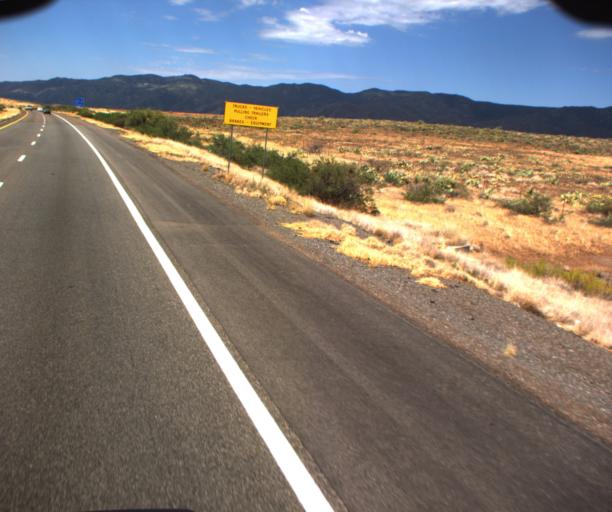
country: US
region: Arizona
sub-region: Yavapai County
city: Cordes Lakes
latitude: 34.2002
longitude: -112.1273
